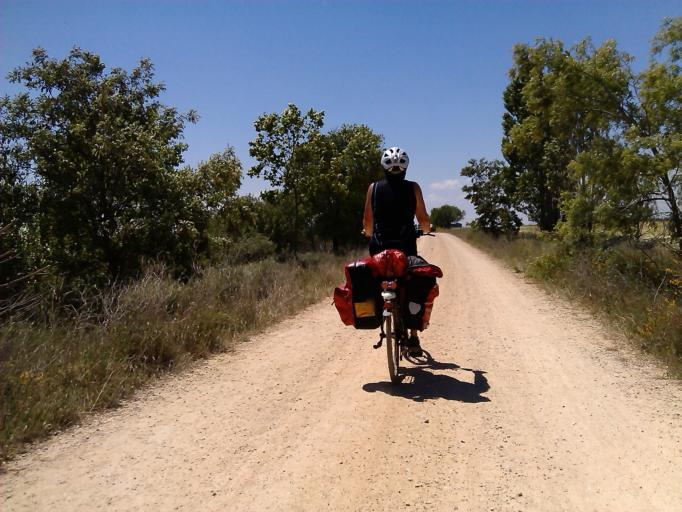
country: ES
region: Castille and Leon
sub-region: Provincia de Palencia
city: Villaturde
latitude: 42.3416
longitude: -4.6931
